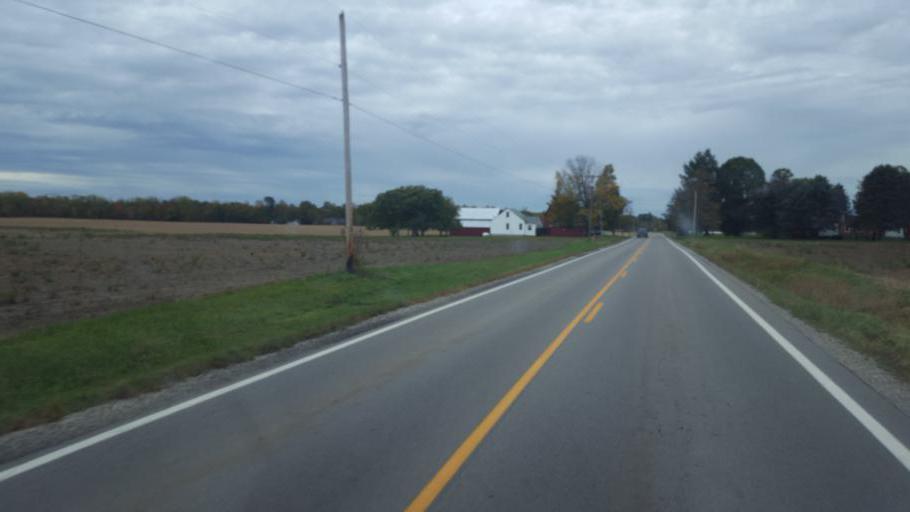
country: US
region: Ohio
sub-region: Huron County
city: Wakeman
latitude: 41.2412
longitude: -82.3951
